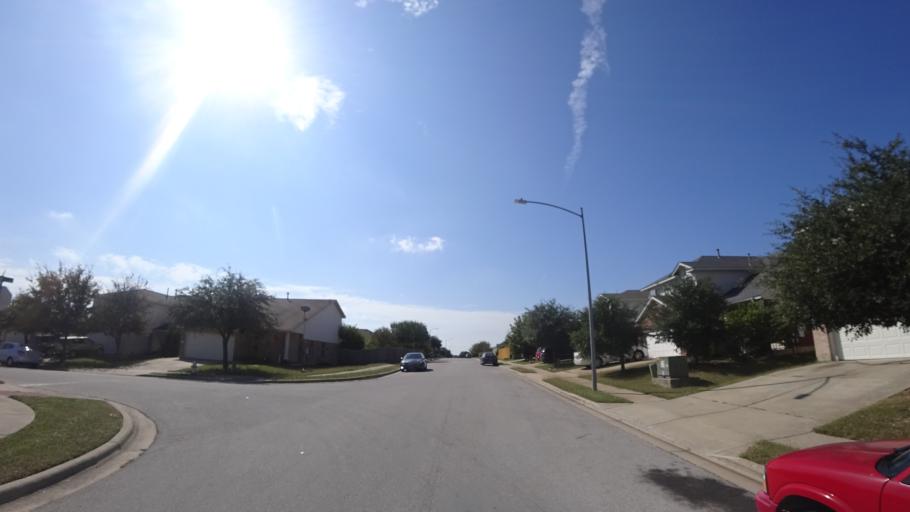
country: US
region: Texas
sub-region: Travis County
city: Pflugerville
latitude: 30.4206
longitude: -97.6319
